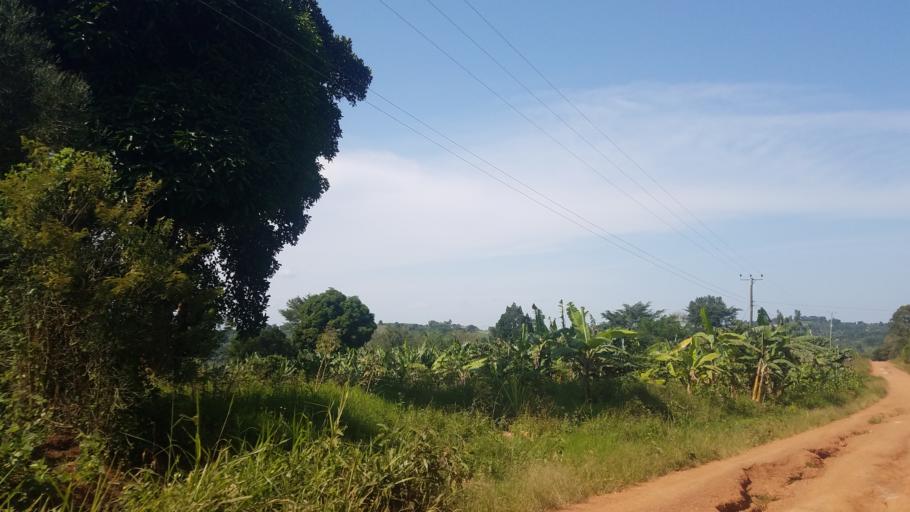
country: UG
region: Central Region
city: Masaka
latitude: -0.3079
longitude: 31.6828
